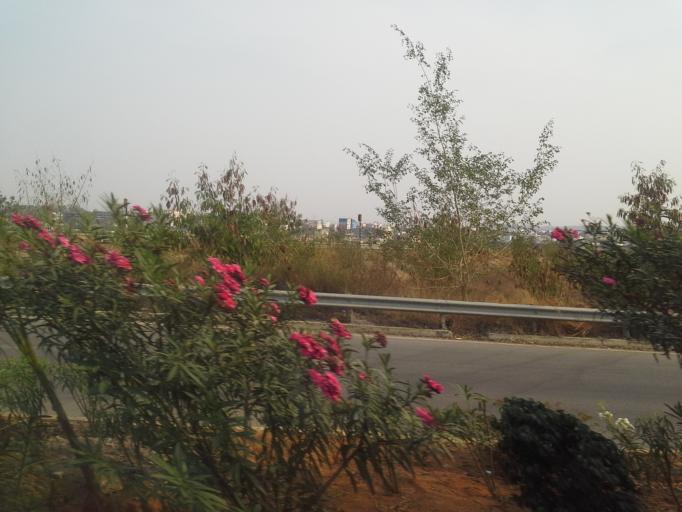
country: IN
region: Telangana
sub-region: Hyderabad
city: Hyderabad
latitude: 17.3975
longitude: 78.3504
